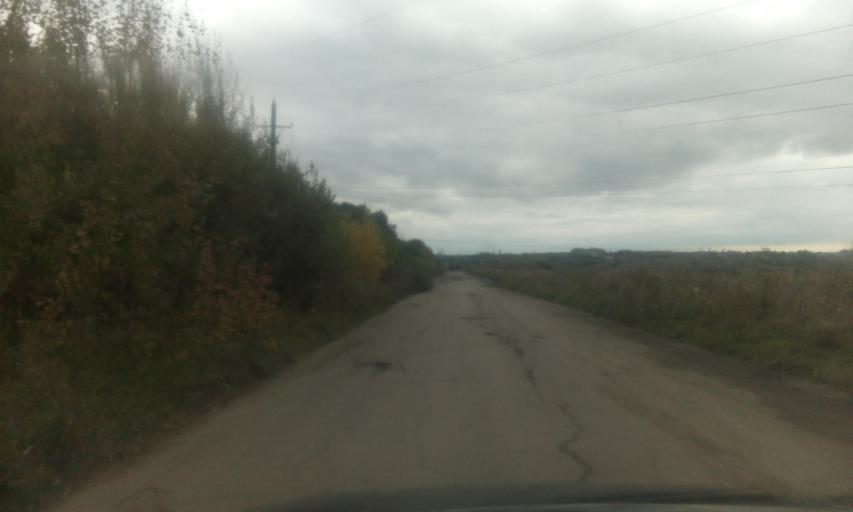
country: RU
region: Tula
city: Gritsovskiy
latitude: 54.1312
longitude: 38.1591
